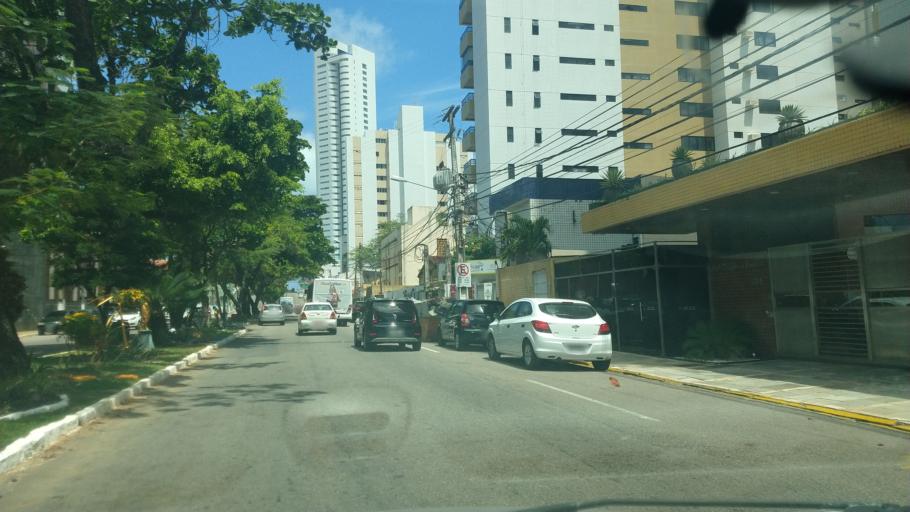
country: BR
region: Rio Grande do Norte
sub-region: Natal
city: Natal
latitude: -5.7828
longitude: -35.1990
